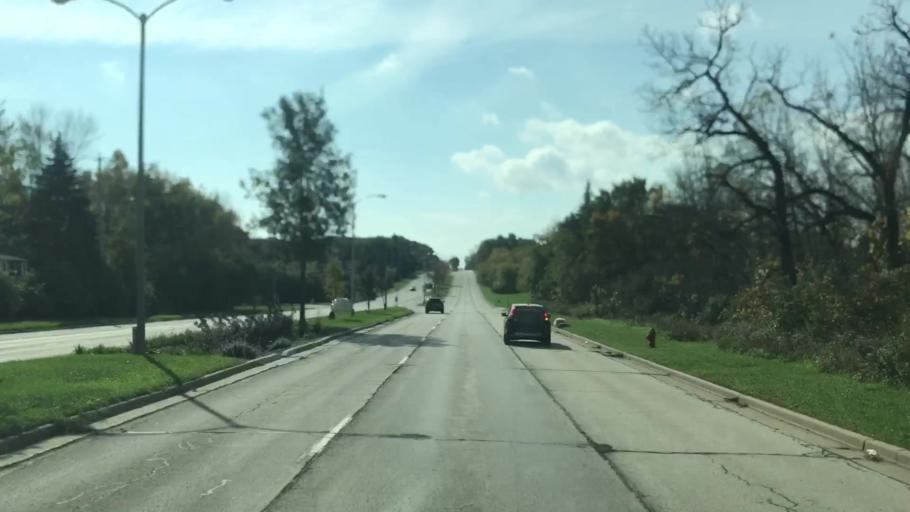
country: US
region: Wisconsin
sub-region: Waukesha County
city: Butler
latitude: 43.1601
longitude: -88.0447
